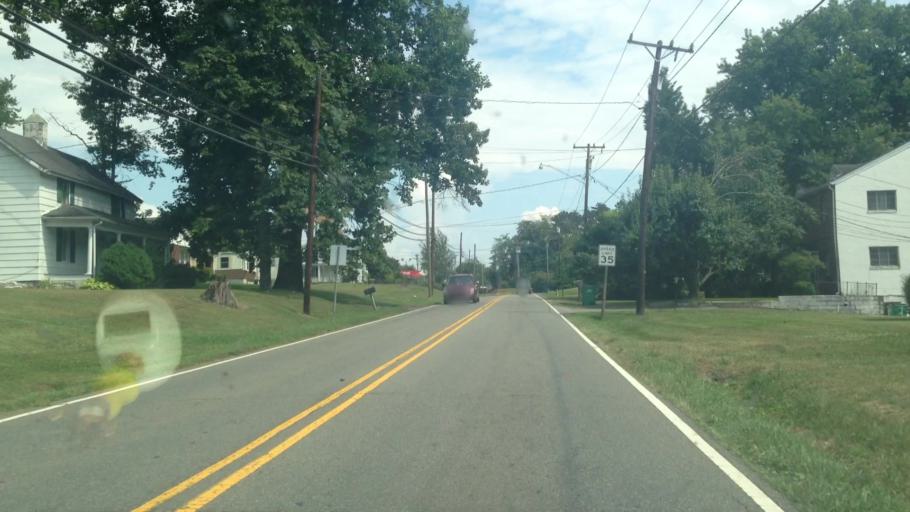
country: US
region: North Carolina
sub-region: Surry County
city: Mount Airy
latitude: 36.4884
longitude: -80.5932
